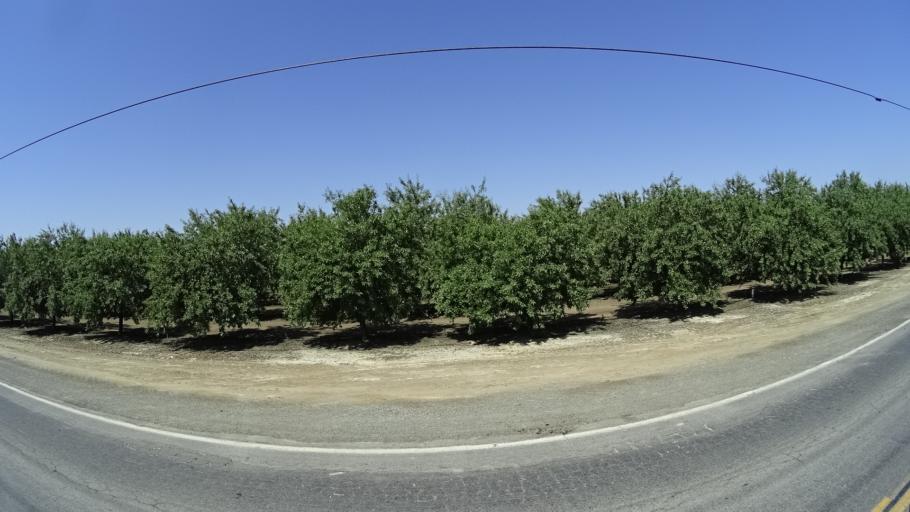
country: US
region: California
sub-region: Kings County
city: Home Garden
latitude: 36.3123
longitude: -119.6190
